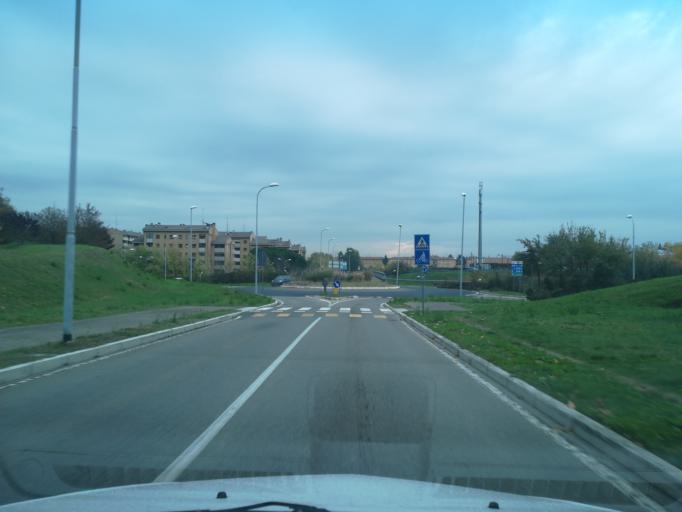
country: IT
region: Emilia-Romagna
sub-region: Provincia di Bologna
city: Imola
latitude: 44.3646
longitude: 11.6967
